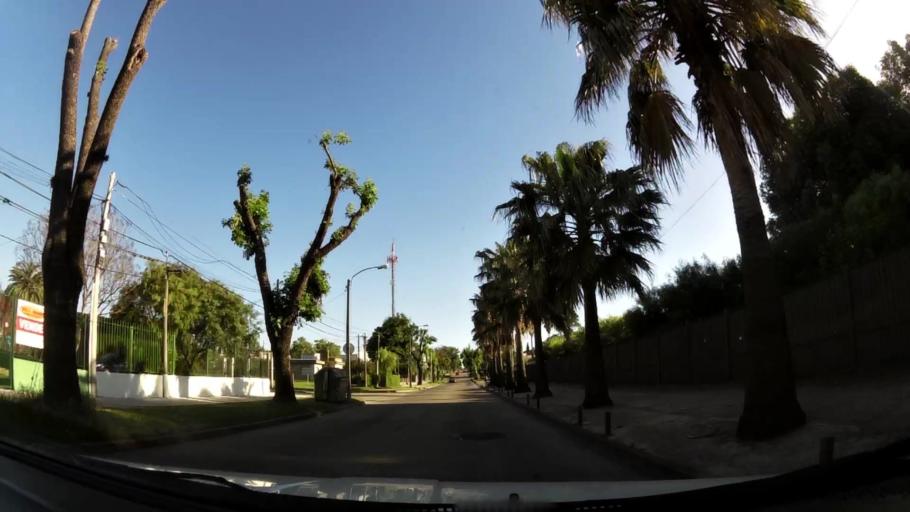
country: UY
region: Montevideo
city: Montevideo
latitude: -34.8318
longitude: -56.2008
